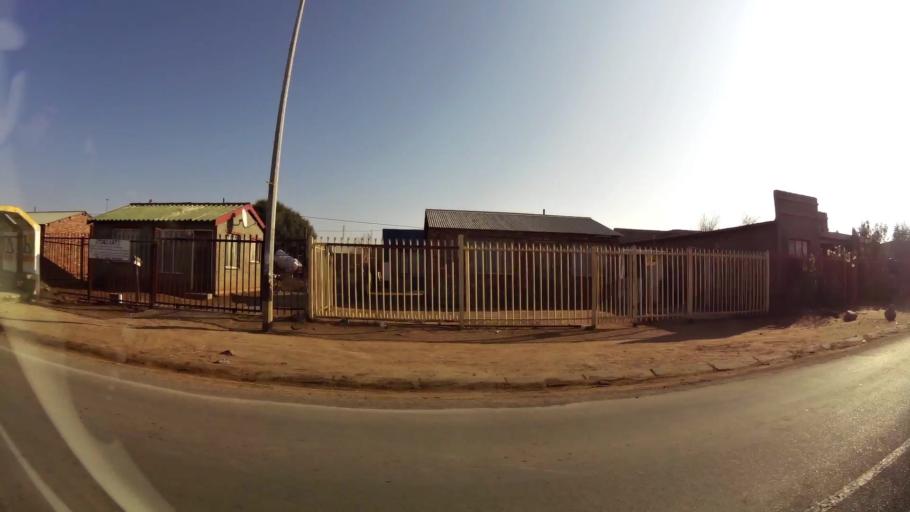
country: ZA
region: Orange Free State
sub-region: Mangaung Metropolitan Municipality
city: Bloemfontein
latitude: -29.2001
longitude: 26.2238
